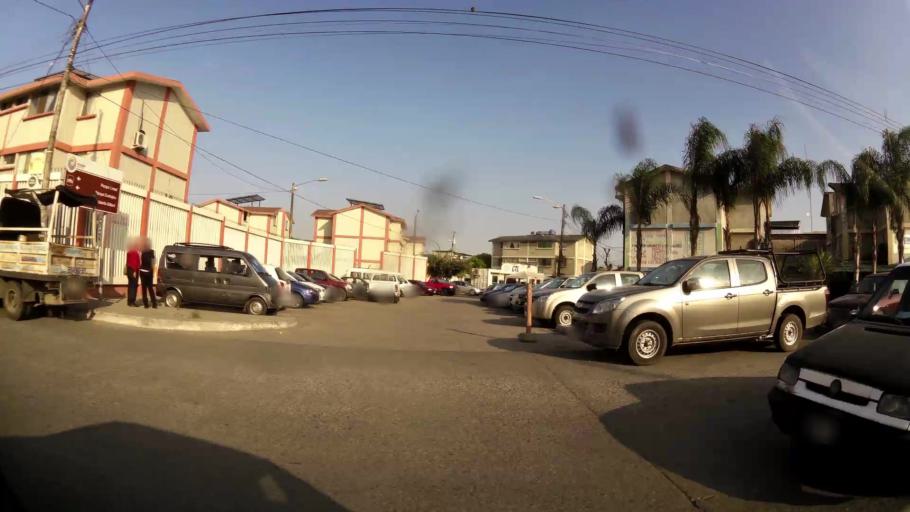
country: EC
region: Guayas
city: Eloy Alfaro
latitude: -2.1779
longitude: -79.8539
